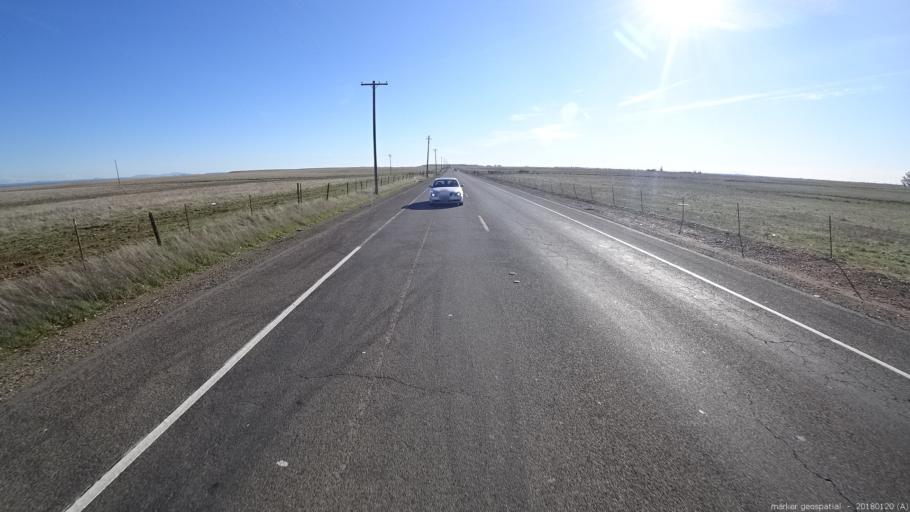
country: US
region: California
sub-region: Sacramento County
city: Gold River
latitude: 38.5556
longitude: -121.1873
